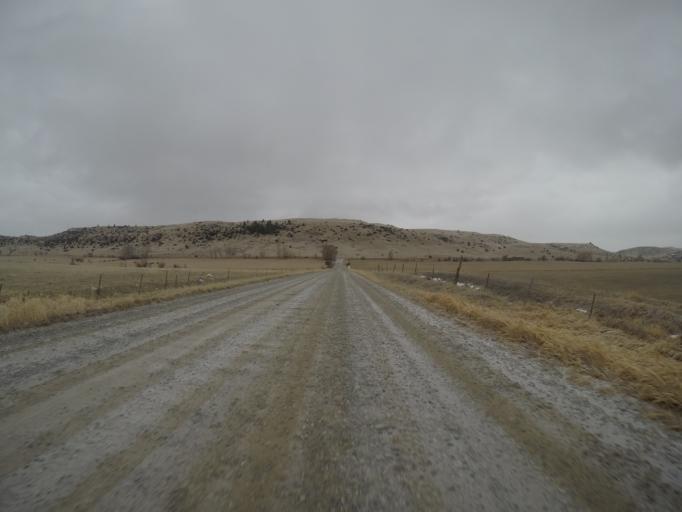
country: US
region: Montana
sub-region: Stillwater County
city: Absarokee
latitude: 45.5253
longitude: -109.4698
